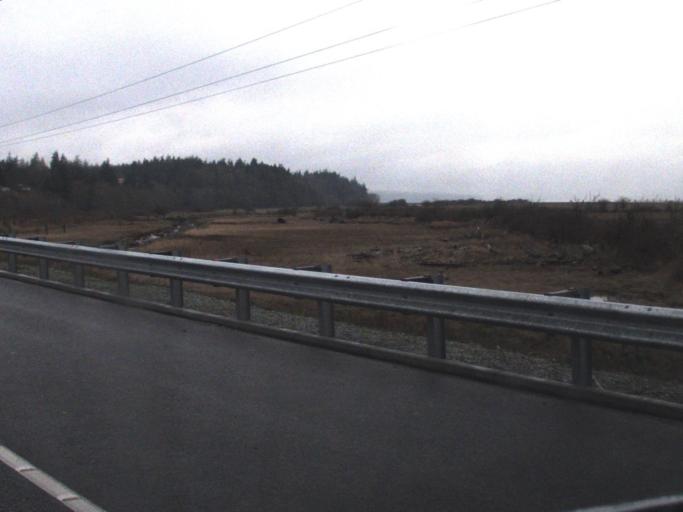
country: US
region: Washington
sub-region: Snohomish County
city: Stanwood
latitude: 48.2398
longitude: -122.3934
